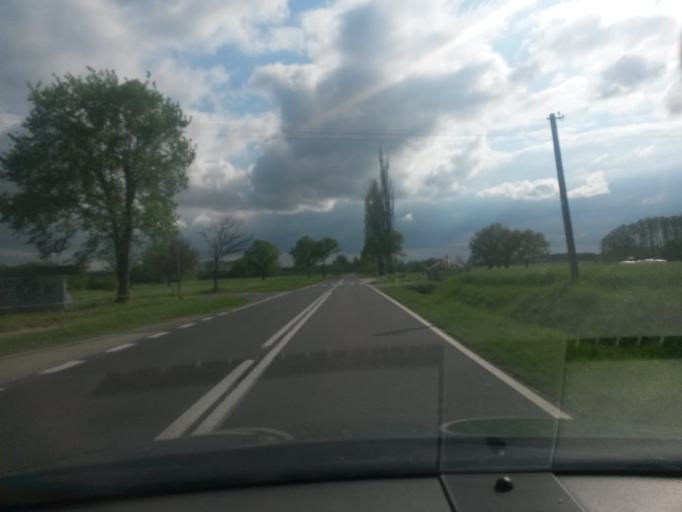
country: PL
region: Masovian Voivodeship
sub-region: Powiat sierpecki
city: Zawidz
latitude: 52.8711
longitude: 19.8600
